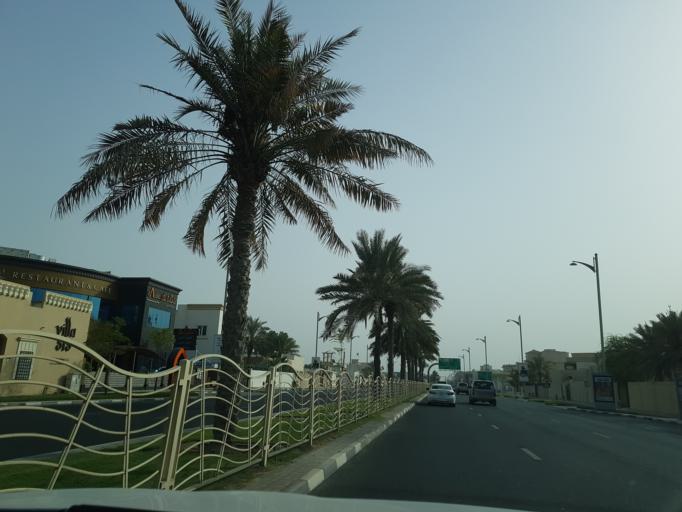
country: AE
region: Dubai
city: Dubai
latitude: 25.1775
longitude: 55.2220
